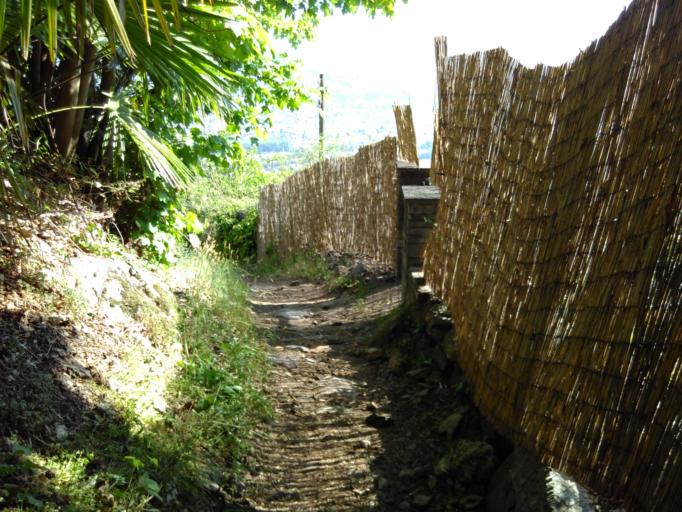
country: CH
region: Ticino
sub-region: Bellinzona District
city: Sementina
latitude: 46.1901
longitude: 8.9917
